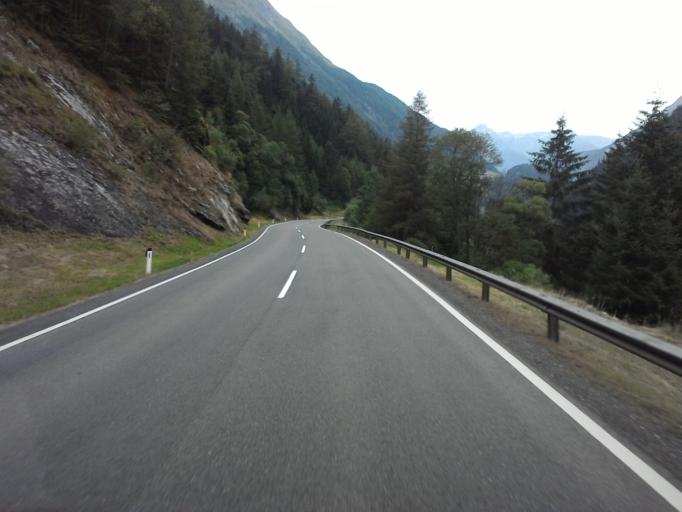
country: AT
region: Tyrol
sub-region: Politischer Bezirk Lienz
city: Matrei in Osttirol
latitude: 47.0819
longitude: 12.5308
